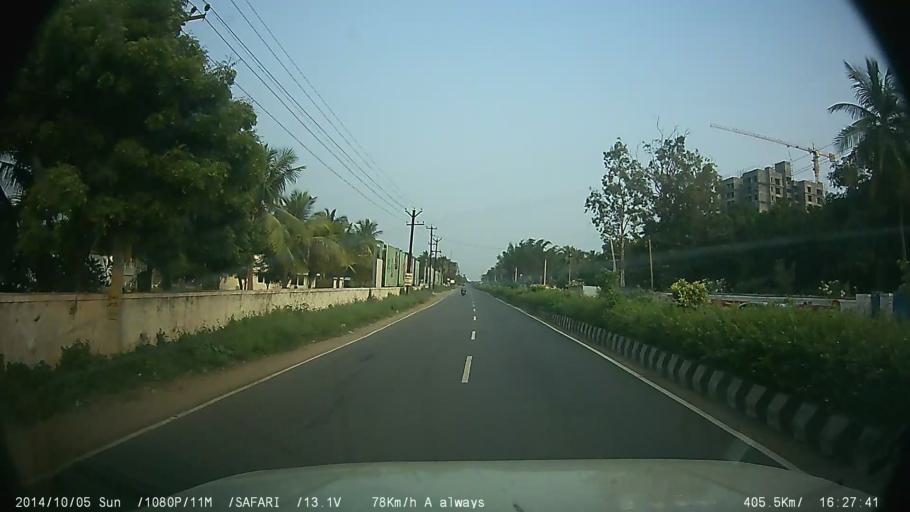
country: IN
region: Tamil Nadu
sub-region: Kancheepuram
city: Vengavasal
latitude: 12.7987
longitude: 80.1994
